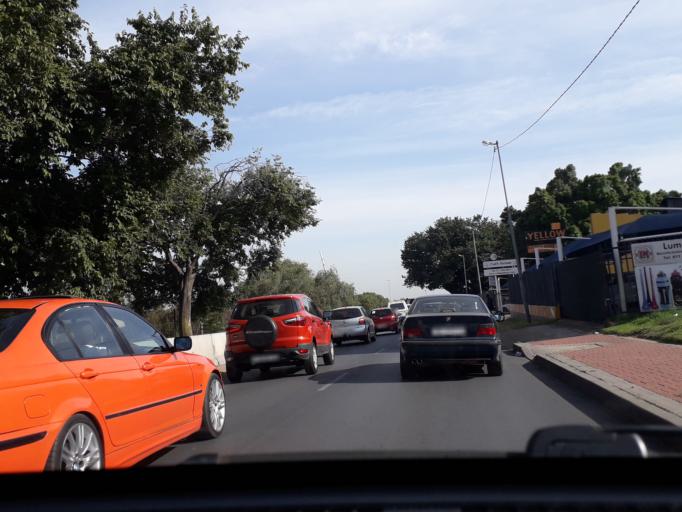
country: ZA
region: Gauteng
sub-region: City of Johannesburg Metropolitan Municipality
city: Modderfontein
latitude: -26.1119
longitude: 28.0782
